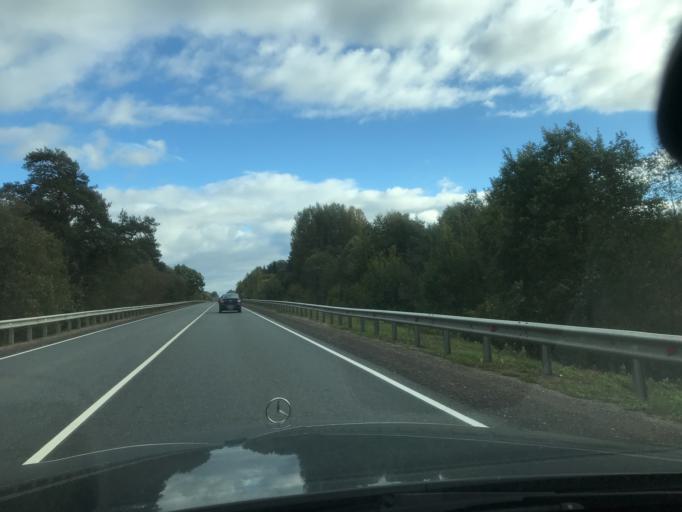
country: RU
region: Pskov
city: Opochka
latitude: 56.6572
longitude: 28.7541
